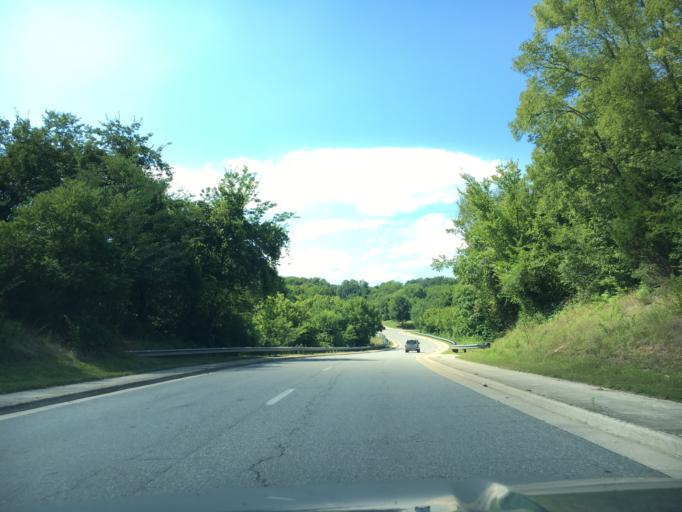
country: US
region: Virginia
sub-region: Halifax County
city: South Boston
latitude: 36.7028
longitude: -78.9032
